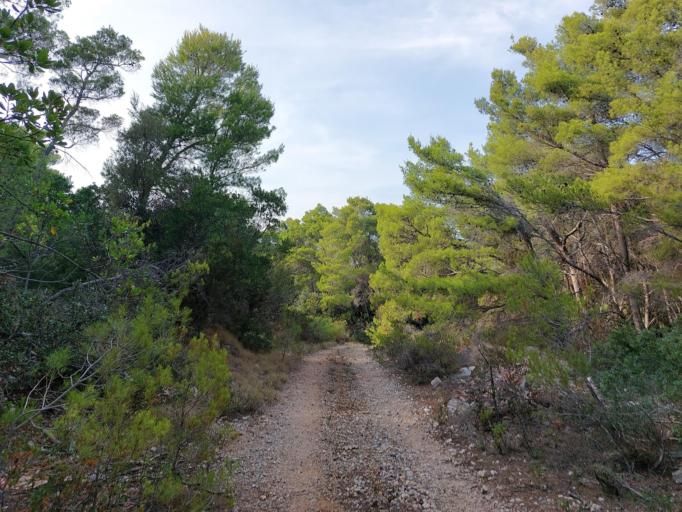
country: HR
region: Dubrovacko-Neretvanska
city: Smokvica
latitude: 42.7351
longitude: 16.8319
